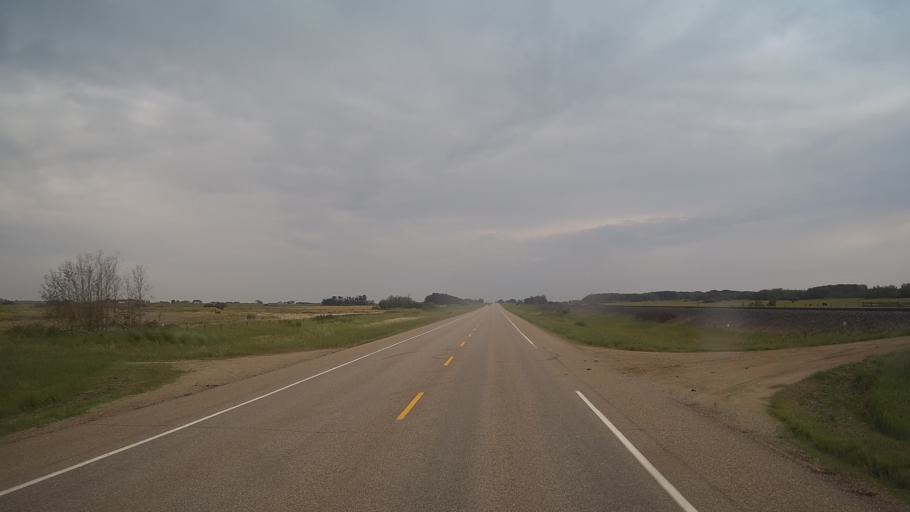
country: CA
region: Saskatchewan
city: Langham
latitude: 52.1271
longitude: -107.2648
